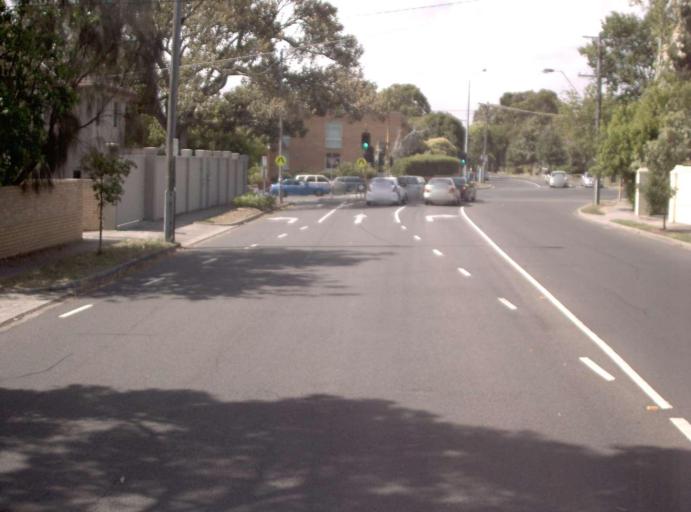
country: AU
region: Victoria
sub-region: Boroondara
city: Hawthorn East
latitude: -37.8164
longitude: 145.0462
